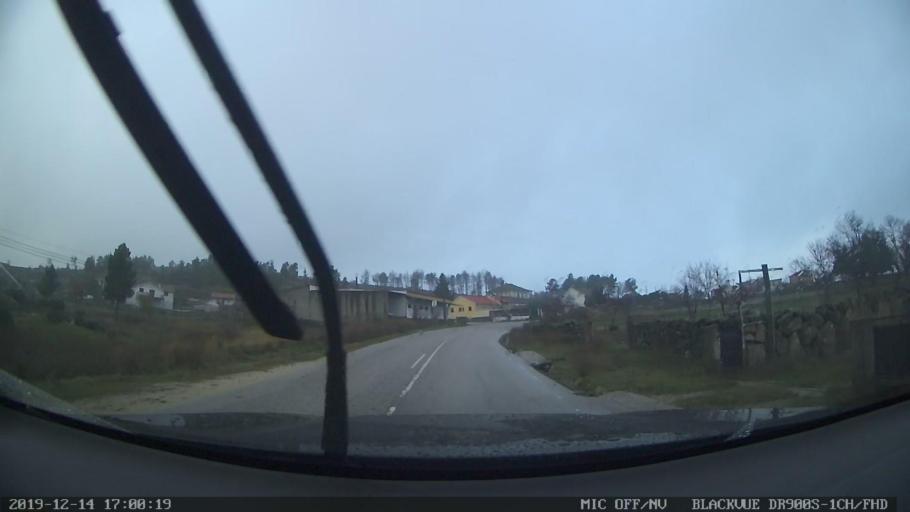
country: PT
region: Vila Real
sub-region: Vila Pouca de Aguiar
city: Vila Pouca de Aguiar
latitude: 41.4396
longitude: -7.5713
